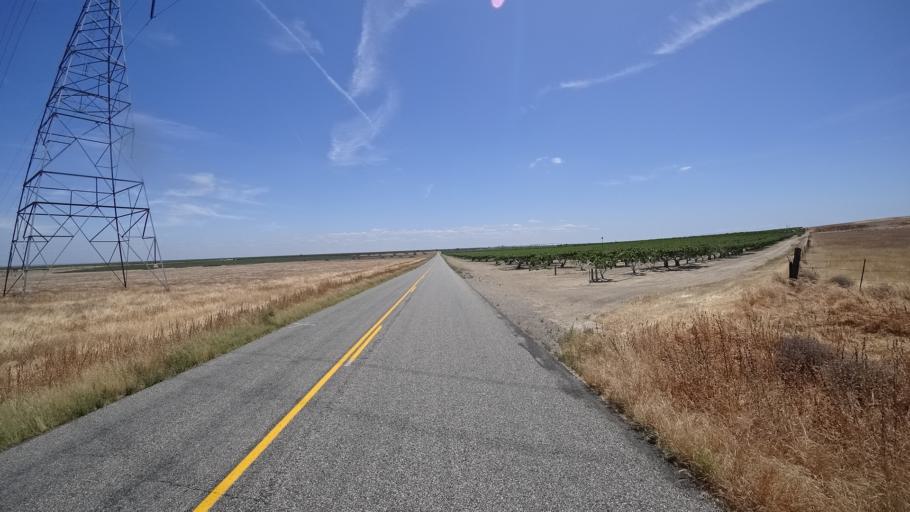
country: US
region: California
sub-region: Kings County
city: Kettleman City
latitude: 35.7868
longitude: -119.8856
